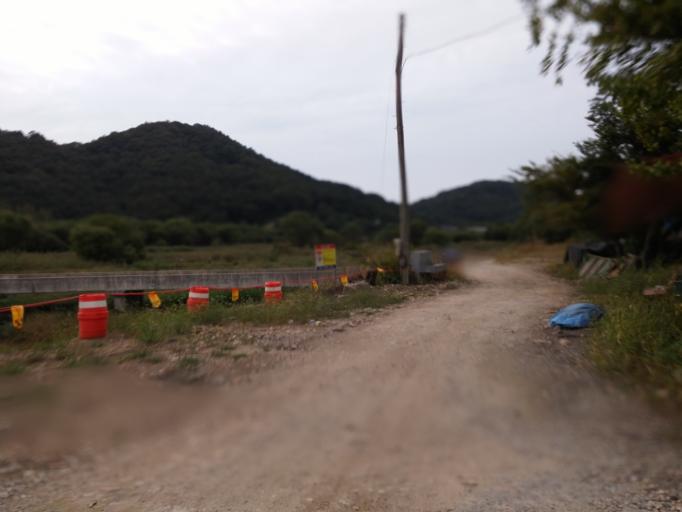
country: KR
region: Chungcheongnam-do
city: Yonmu
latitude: 36.1564
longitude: 127.2035
